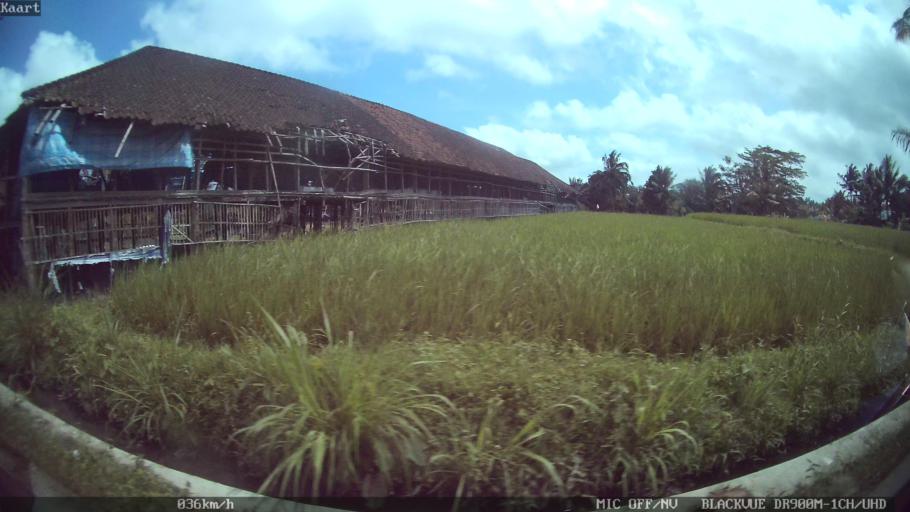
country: ID
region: Bali
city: Banjar Abuan
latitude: -8.4692
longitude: 115.3424
